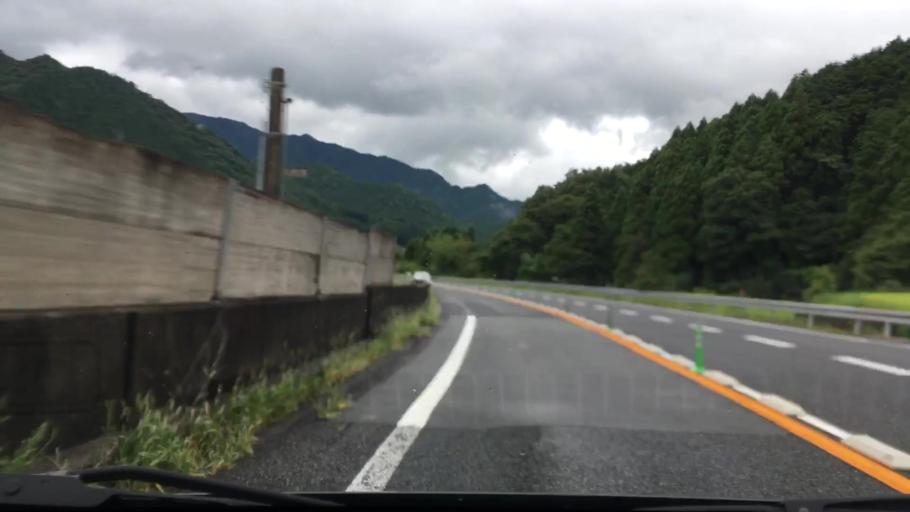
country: JP
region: Hyogo
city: Nishiwaki
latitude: 35.0938
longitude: 134.7758
